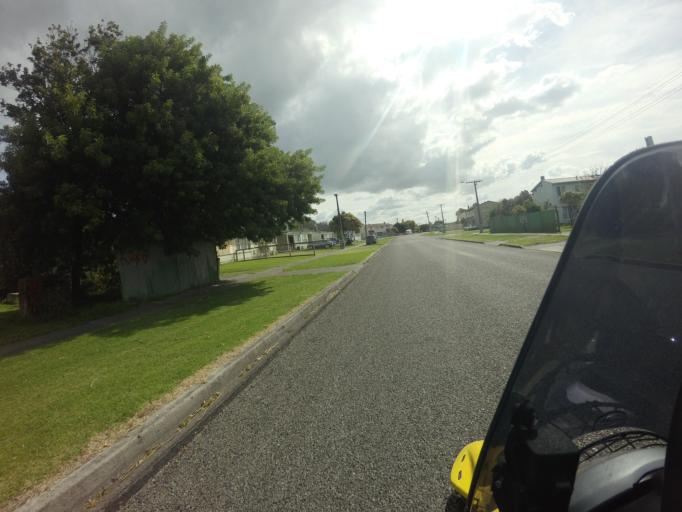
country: NZ
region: Gisborne
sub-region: Gisborne District
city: Gisborne
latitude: -38.6766
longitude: 178.0416
